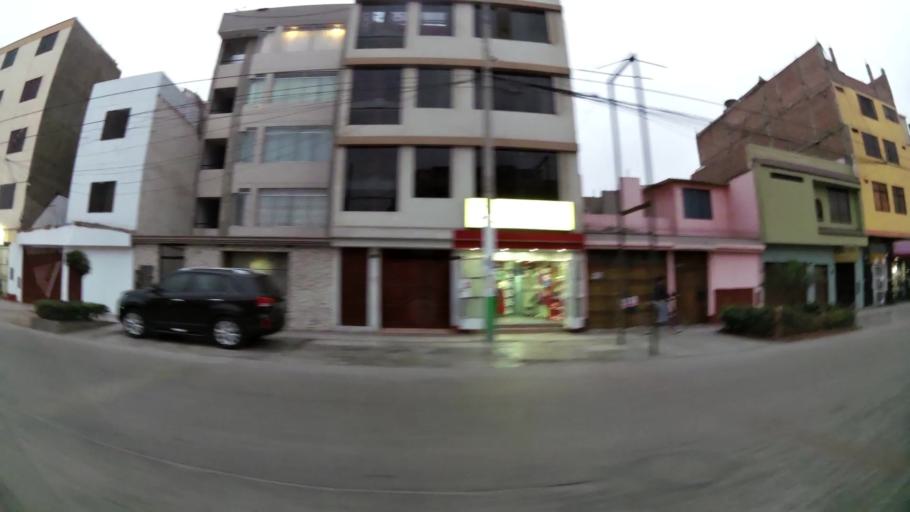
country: PE
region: Callao
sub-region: Callao
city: Callao
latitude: -12.0725
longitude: -77.1118
